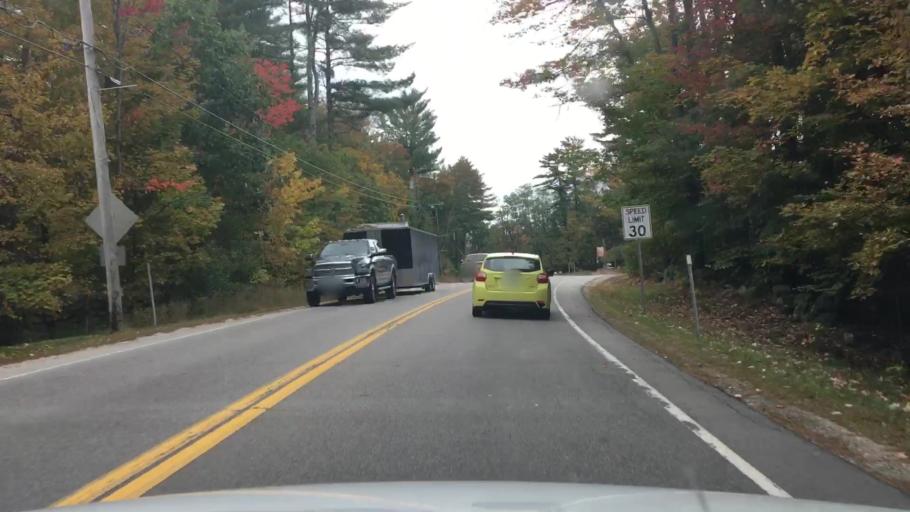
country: US
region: New Hampshire
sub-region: Carroll County
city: Tamworth
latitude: 43.8814
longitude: -71.2233
